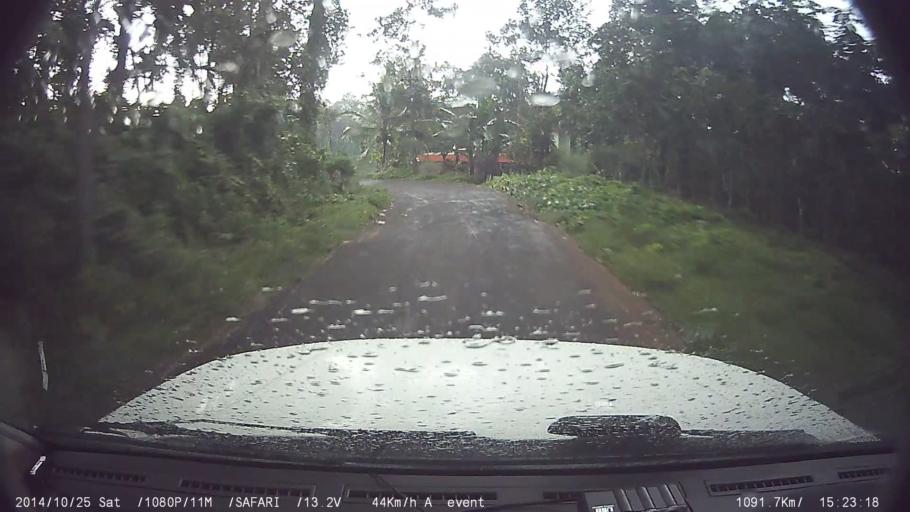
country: IN
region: Kerala
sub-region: Kottayam
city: Palackattumala
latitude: 9.7833
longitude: 76.5644
